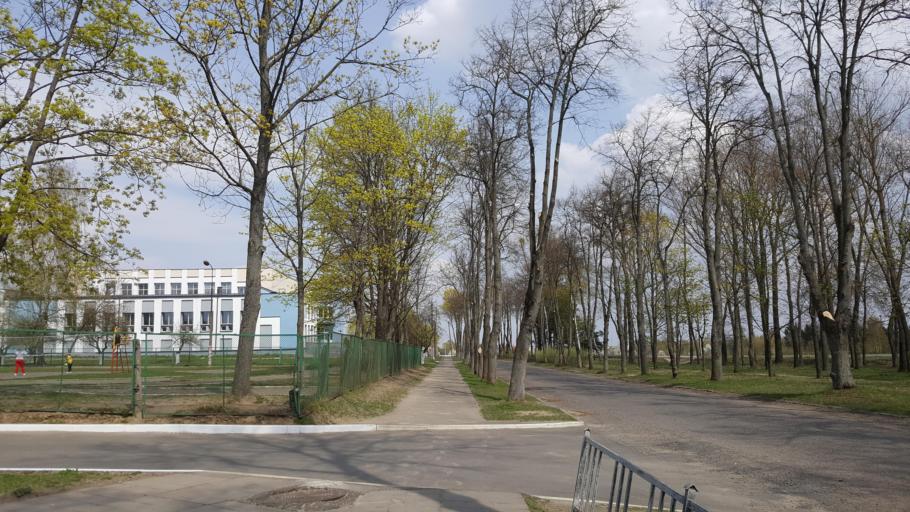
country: BY
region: Brest
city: Zhabinka
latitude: 52.1913
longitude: 23.9870
